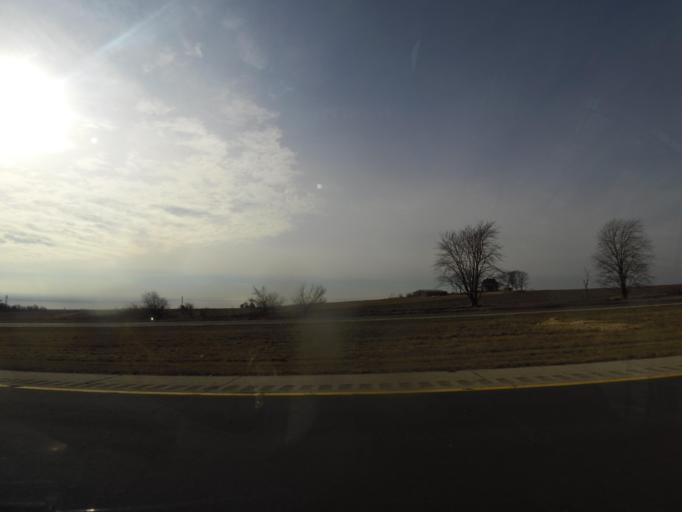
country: US
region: Illinois
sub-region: Macon County
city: Decatur
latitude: 39.7931
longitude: -88.9970
